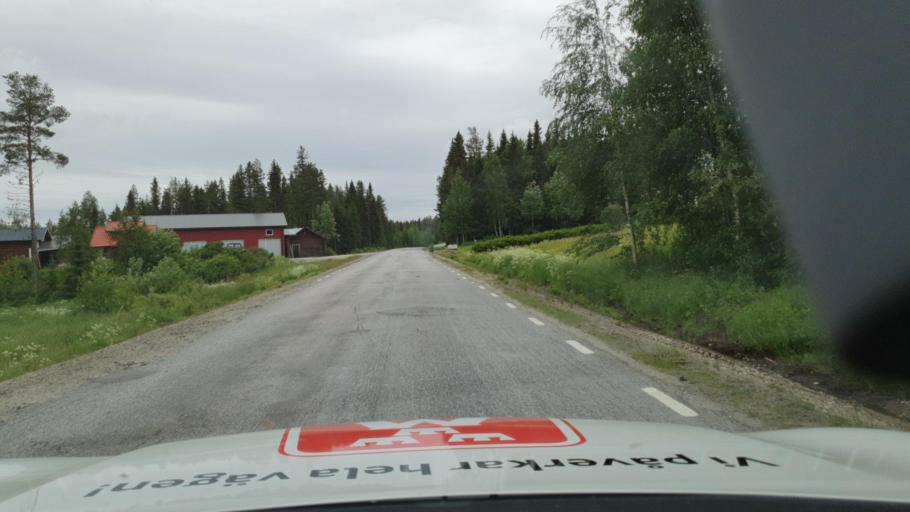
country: SE
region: Vaesterbotten
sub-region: Lycksele Kommun
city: Lycksele
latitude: 64.1380
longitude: 18.3606
